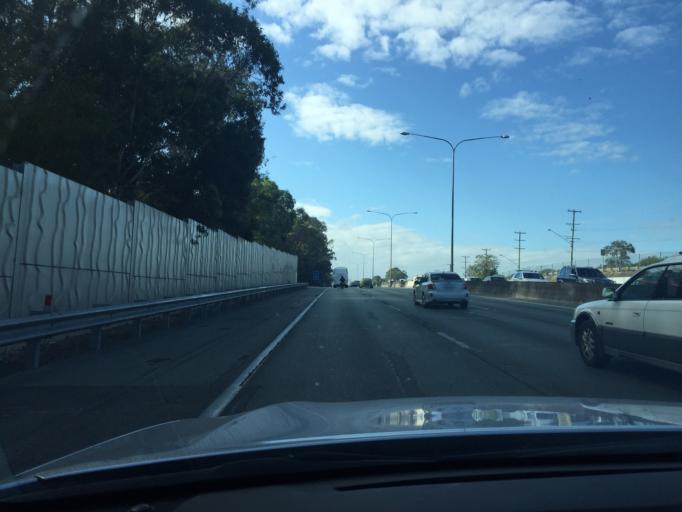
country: AU
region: Queensland
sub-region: Logan
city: Slacks Creek
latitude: -27.6502
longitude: 153.1585
